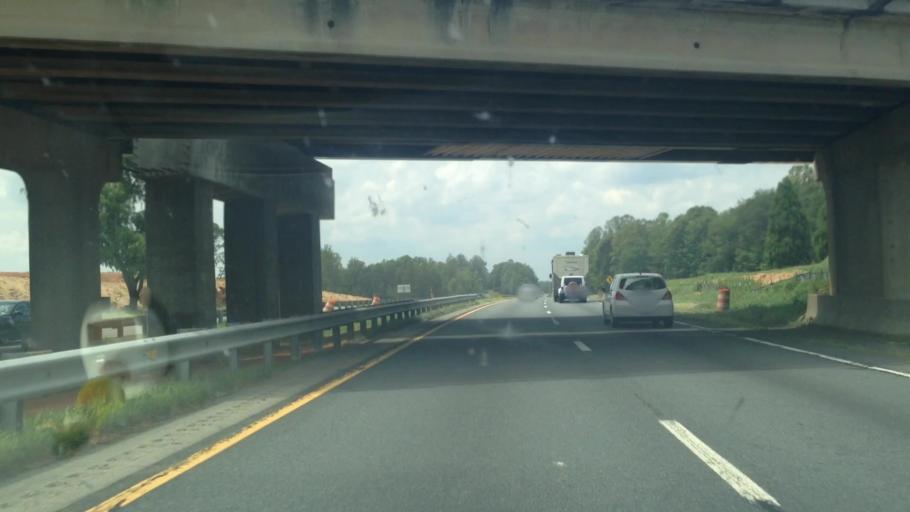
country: US
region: North Carolina
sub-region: Forsyth County
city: Rural Hall
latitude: 36.2105
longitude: -80.3031
